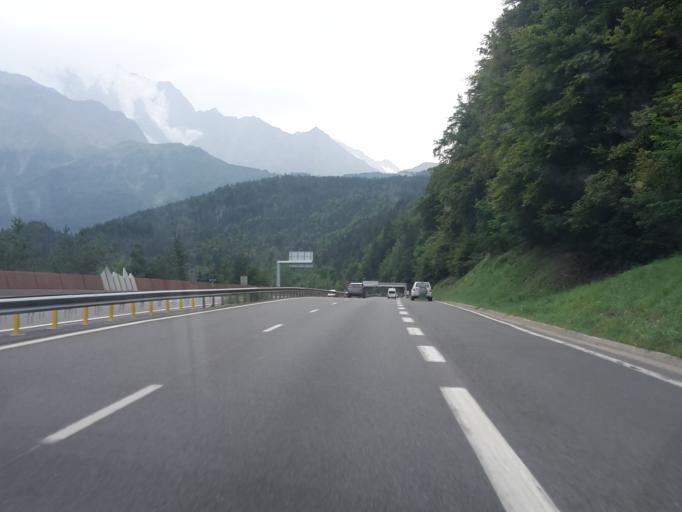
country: FR
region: Rhone-Alpes
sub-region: Departement de la Haute-Savoie
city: Les Houches
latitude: 45.9228
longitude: 6.7627
